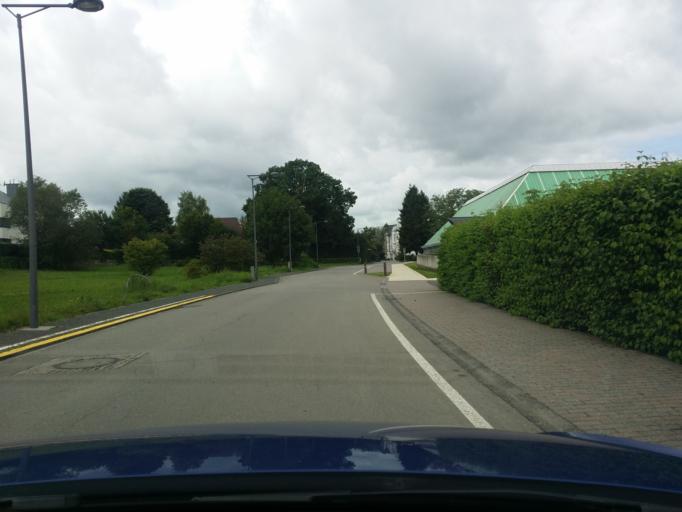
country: LU
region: Luxembourg
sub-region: Canton de Luxembourg
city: Bertrange
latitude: 49.6090
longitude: 6.0543
